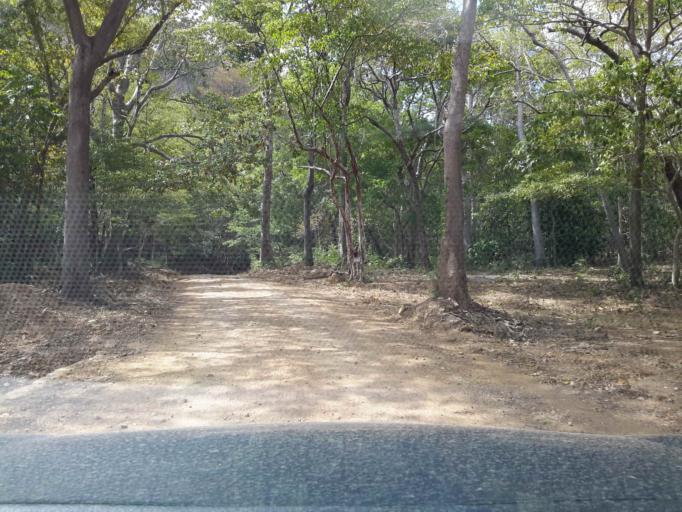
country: NI
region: Rivas
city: San Juan del Sur
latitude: 11.2177
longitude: -85.8334
